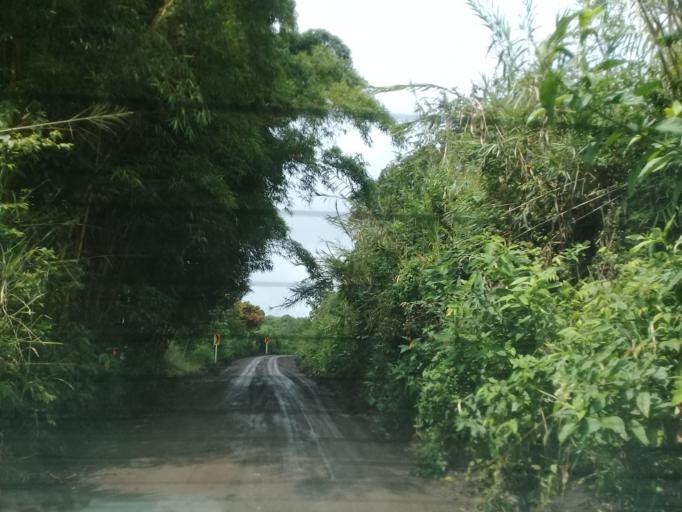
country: CO
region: Cundinamarca
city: Quipile
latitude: 4.7067
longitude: -74.5308
